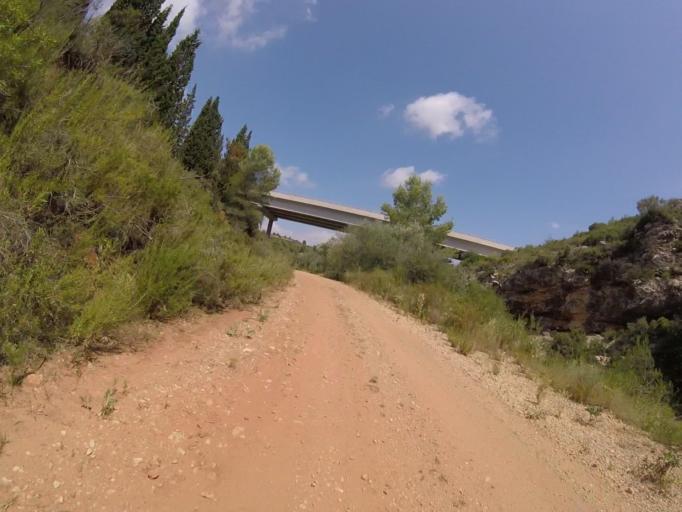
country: ES
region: Valencia
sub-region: Provincia de Castello
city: Torreblanca
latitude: 40.2096
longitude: 0.1403
